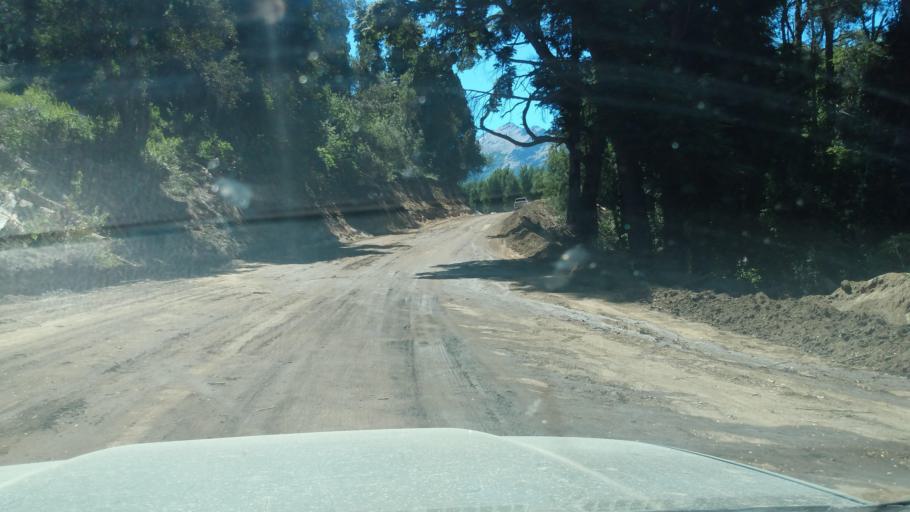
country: AR
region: Neuquen
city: Villa La Angostura
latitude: -40.6258
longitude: -71.5000
